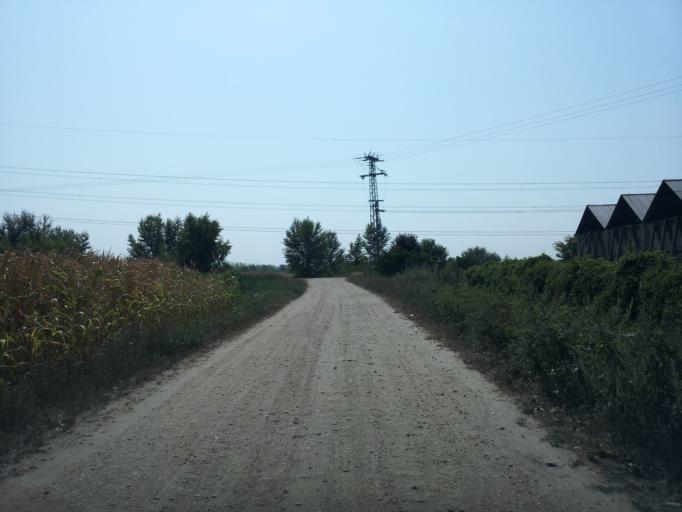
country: HU
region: Pest
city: Dunavarsany
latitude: 47.2819
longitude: 19.0421
